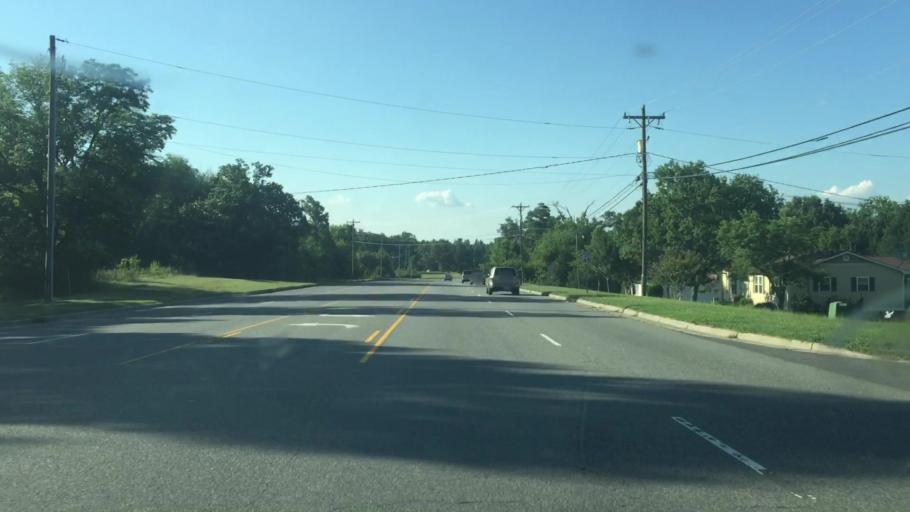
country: US
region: North Carolina
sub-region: Cabarrus County
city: Kannapolis
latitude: 35.4313
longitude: -80.6799
